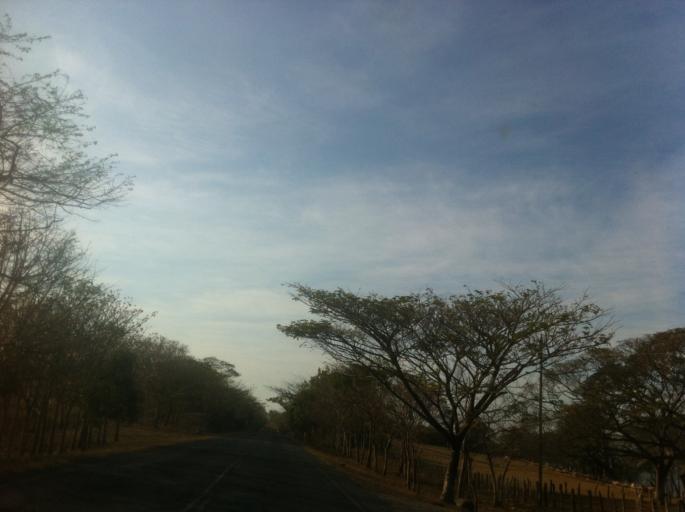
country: NI
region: Rivas
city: Cardenas
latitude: 11.2848
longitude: -85.6754
